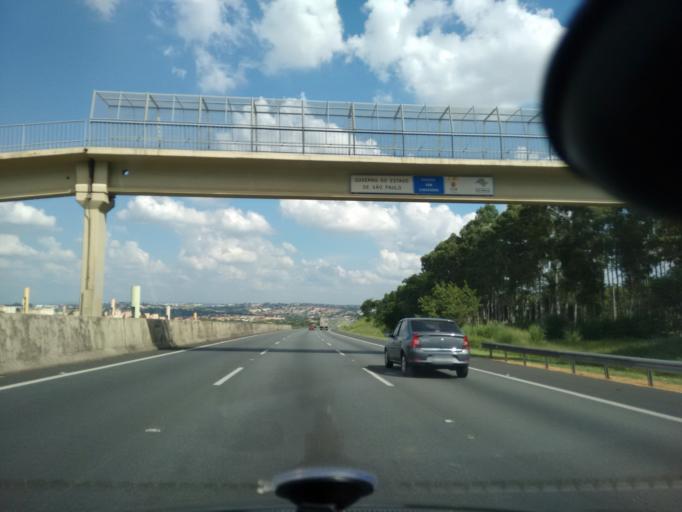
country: BR
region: Sao Paulo
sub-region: Campinas
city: Campinas
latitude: -22.9406
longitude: -47.1264
